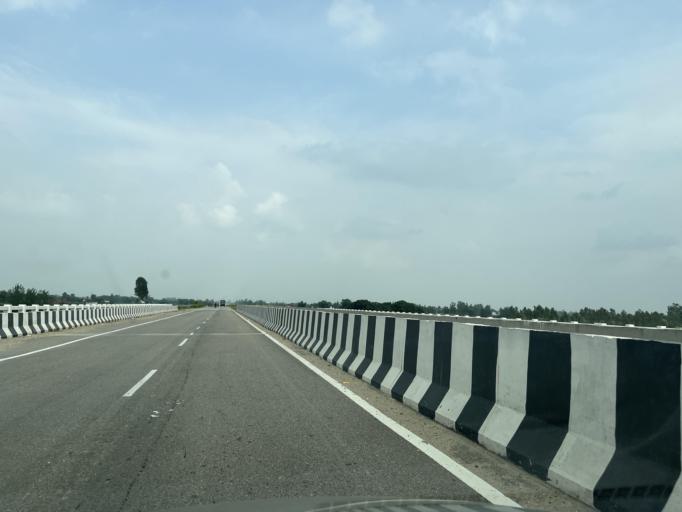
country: IN
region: Uttarakhand
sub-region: Udham Singh Nagar
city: Bazpur
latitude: 29.1473
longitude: 79.0400
